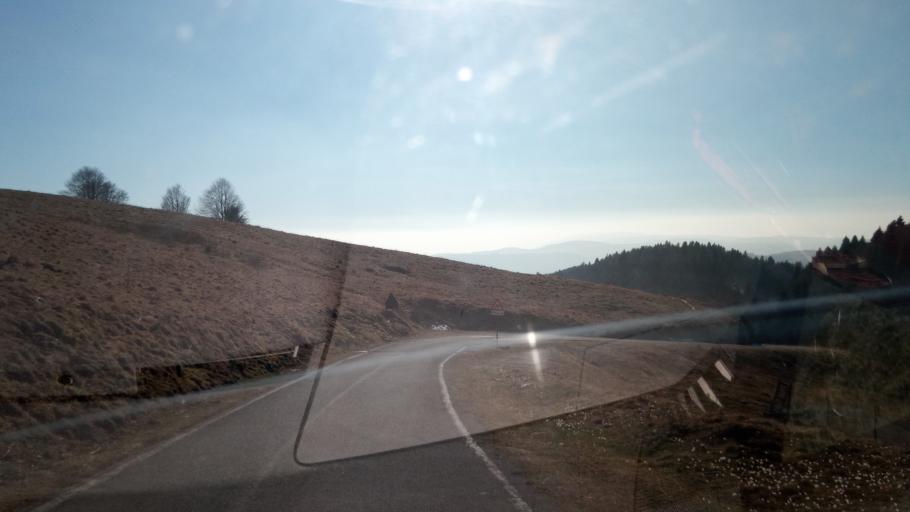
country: IT
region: Veneto
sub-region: Provincia di Treviso
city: Borso del Grappa
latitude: 45.8484
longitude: 11.7934
